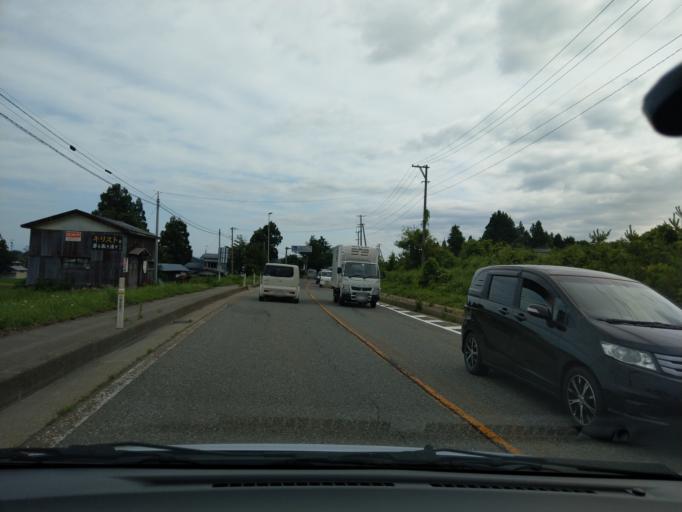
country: JP
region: Akita
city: Yokotemachi
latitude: 39.3551
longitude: 140.5623
